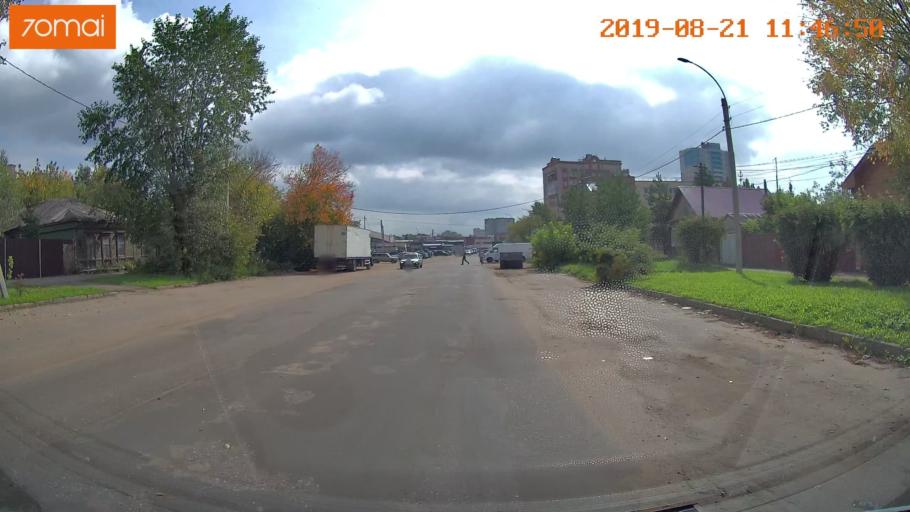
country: RU
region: Ivanovo
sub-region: Gorod Ivanovo
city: Ivanovo
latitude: 56.9907
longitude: 40.9651
